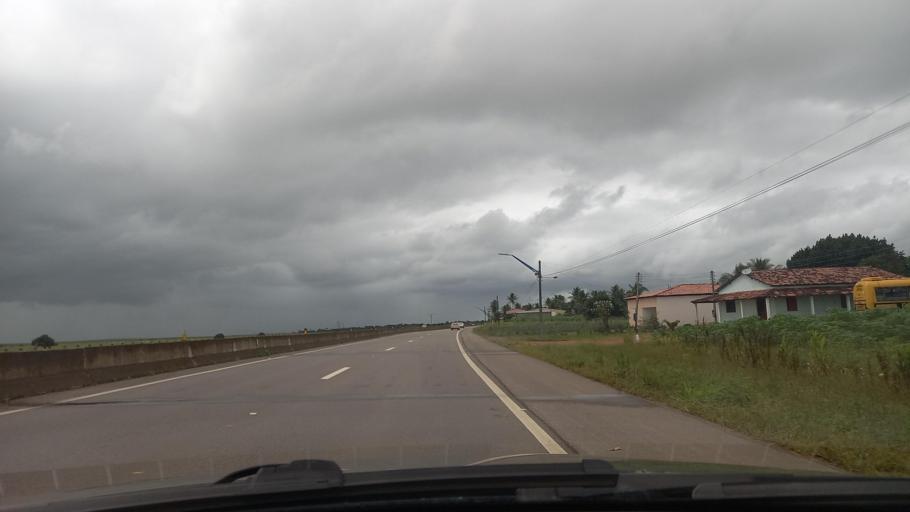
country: BR
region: Alagoas
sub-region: Limoeiro De Anadia
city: Cajueiro
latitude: -9.7434
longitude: -36.4667
